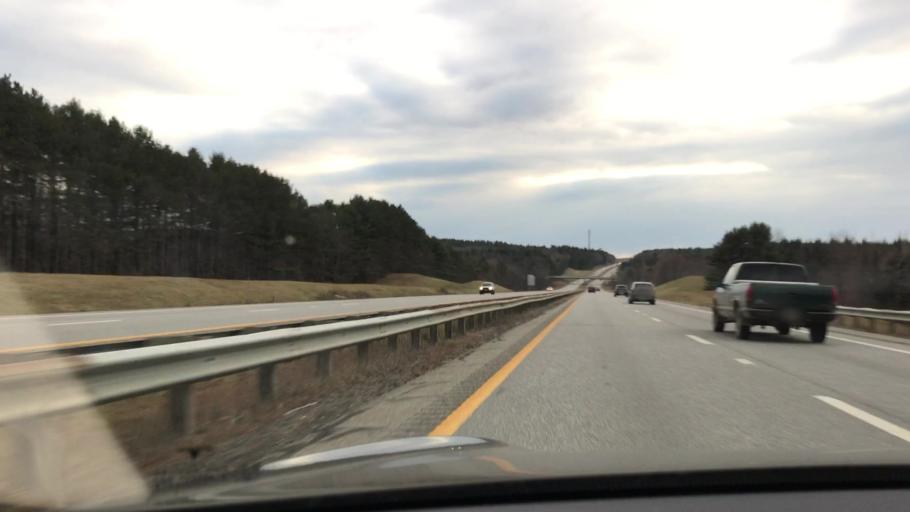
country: US
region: Maine
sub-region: Kennebec County
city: Hallowell
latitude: 44.2834
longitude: -69.8067
